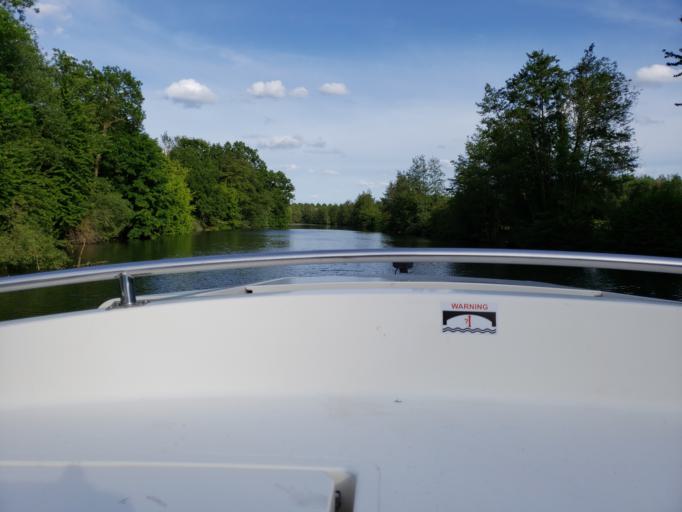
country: FR
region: Bourgogne
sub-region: Departement de l'Yonne
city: Migennes
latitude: 47.9437
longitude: 3.5055
